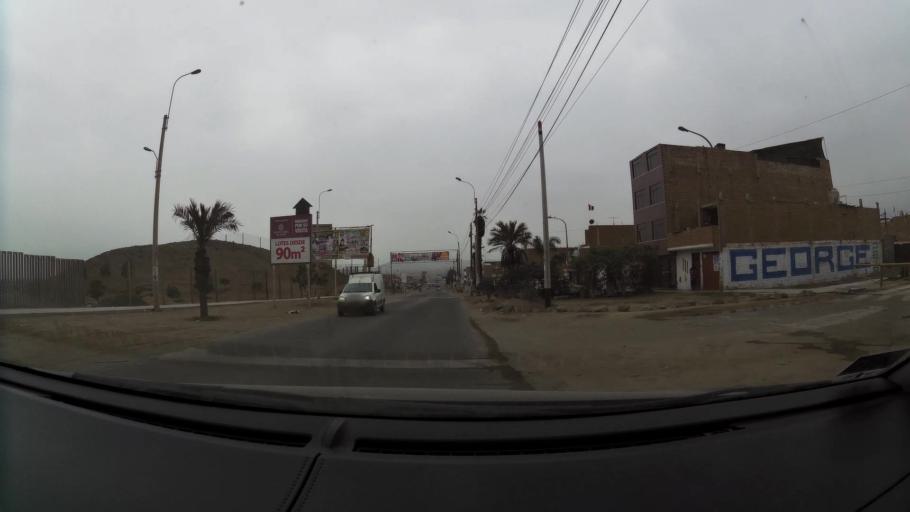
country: PE
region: Lima
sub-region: Lima
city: Santa Rosa
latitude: -11.7882
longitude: -77.1577
